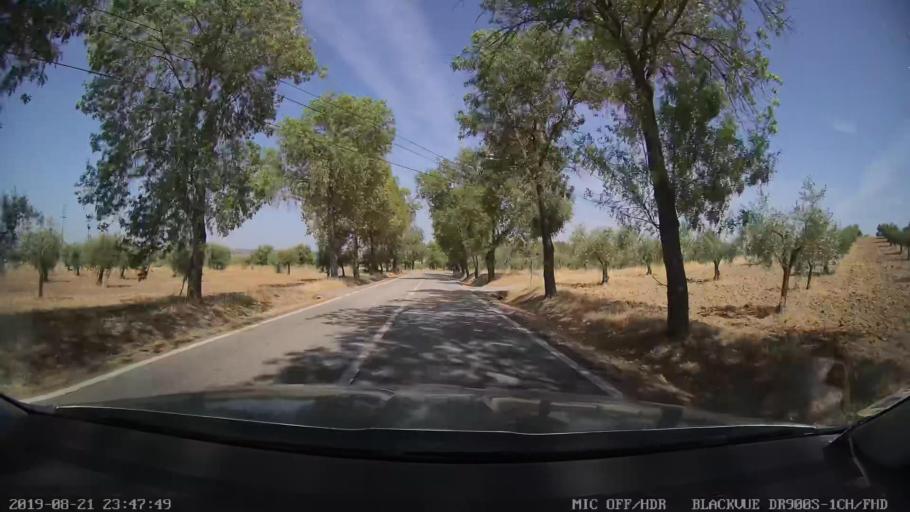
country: PT
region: Castelo Branco
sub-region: Idanha-A-Nova
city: Idanha-a-Nova
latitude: 39.8566
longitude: -7.2589
